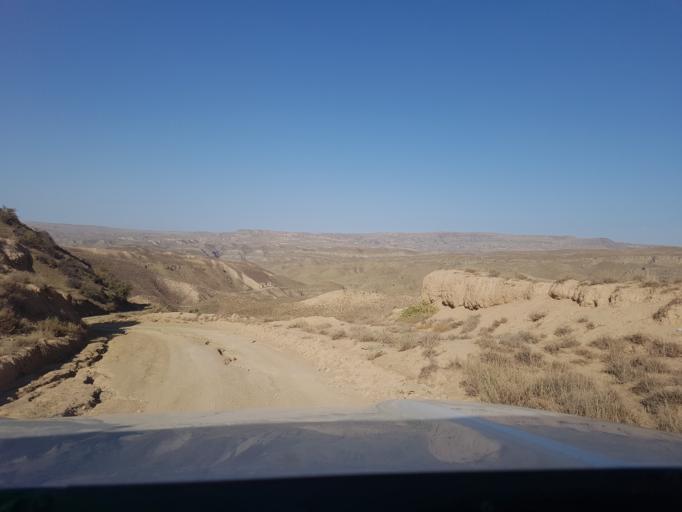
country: TM
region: Balkan
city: Magtymguly
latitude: 38.3008
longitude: 56.7887
